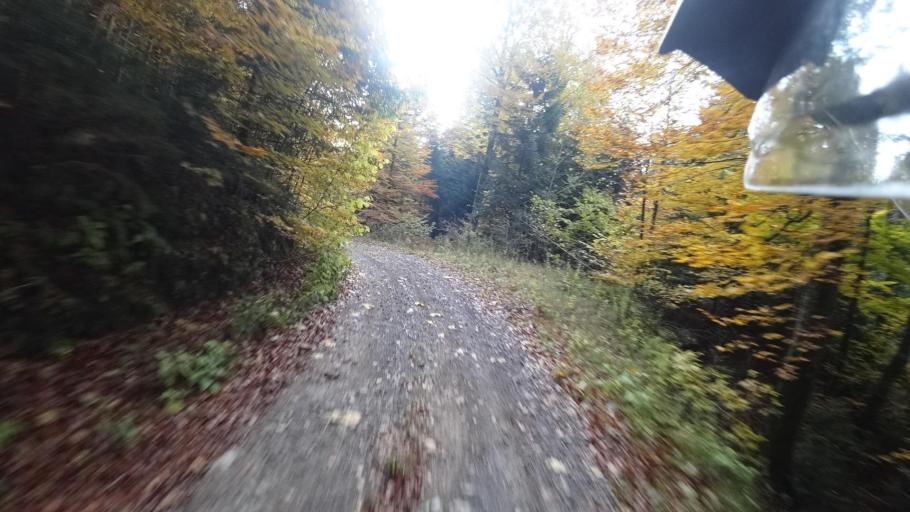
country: HR
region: Karlovacka
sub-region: Grad Ogulin
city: Ogulin
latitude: 45.2069
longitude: 15.1007
